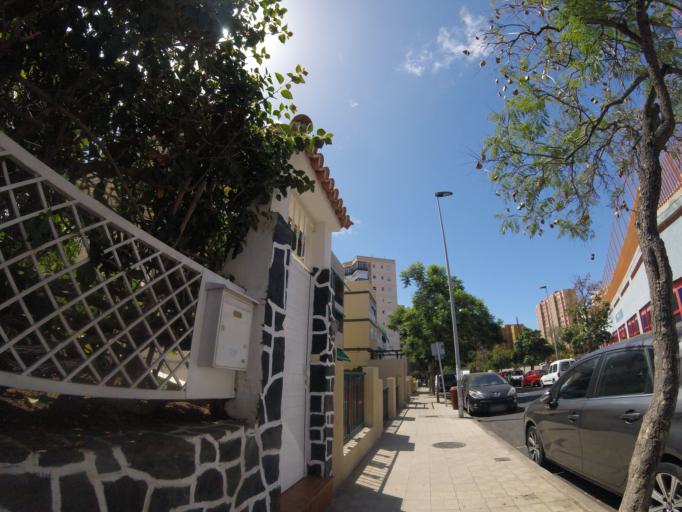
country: ES
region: Canary Islands
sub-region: Provincia de Santa Cruz de Tenerife
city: Santa Cruz de Tenerife
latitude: 28.4623
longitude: -16.2591
